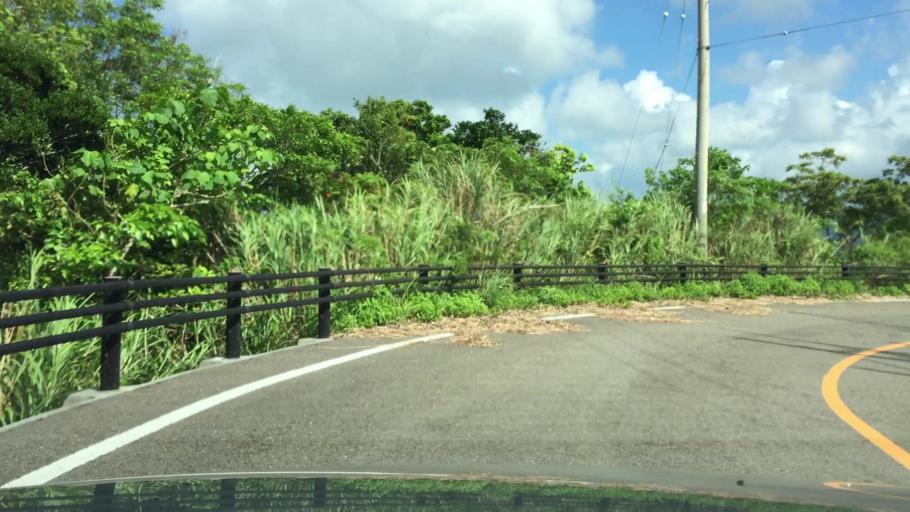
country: JP
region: Okinawa
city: Ishigaki
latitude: 24.3802
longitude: 124.1647
